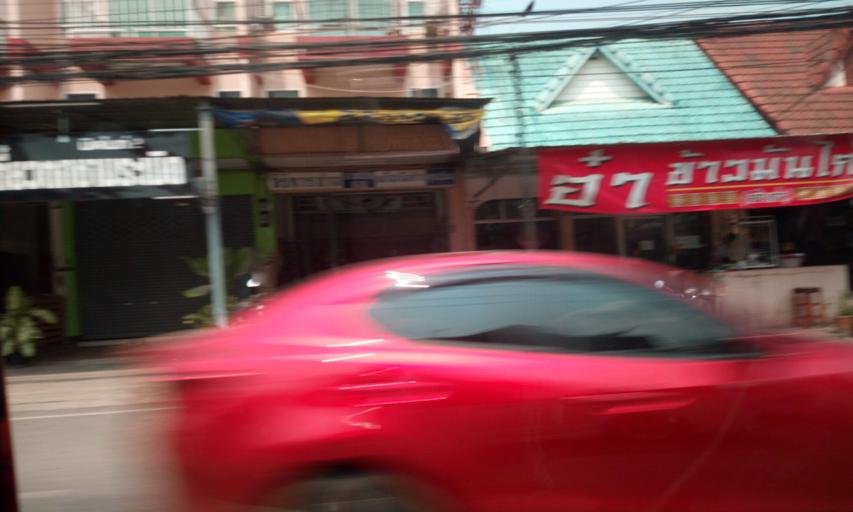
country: TH
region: Chiang Rai
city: Chiang Rai
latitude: 19.8892
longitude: 99.8303
